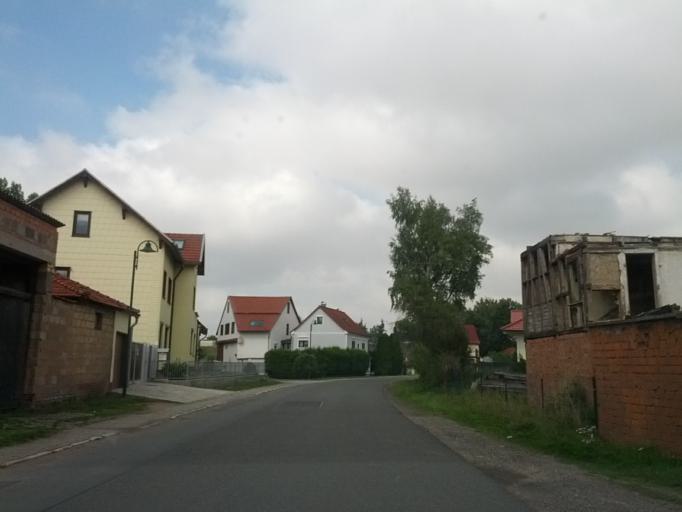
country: DE
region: Thuringia
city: Ernstroda
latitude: 50.9049
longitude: 10.6314
